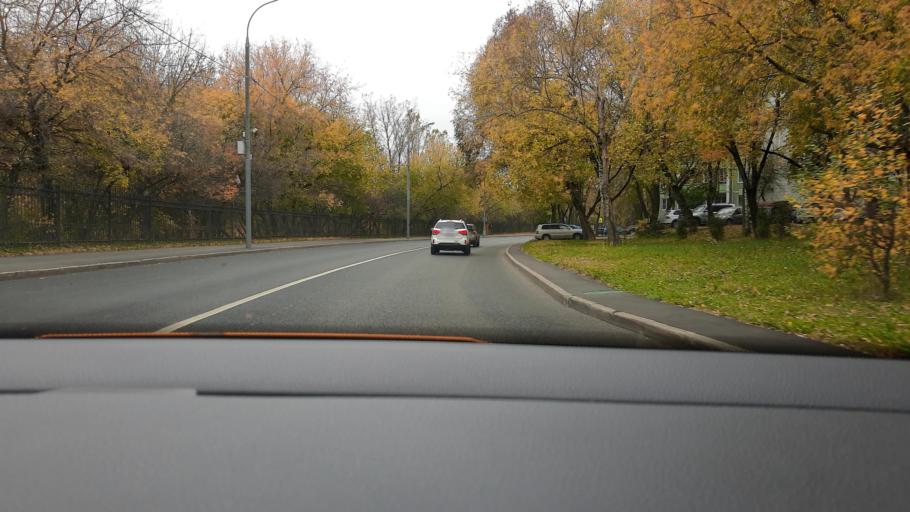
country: RU
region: Moscow
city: Leonovo
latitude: 55.8689
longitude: 37.6468
